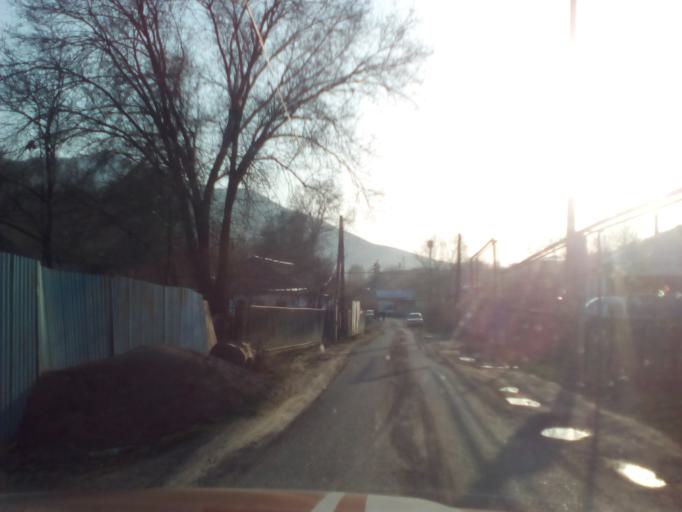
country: KZ
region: Almaty Oblysy
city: Burunday
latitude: 43.1573
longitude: 76.4357
